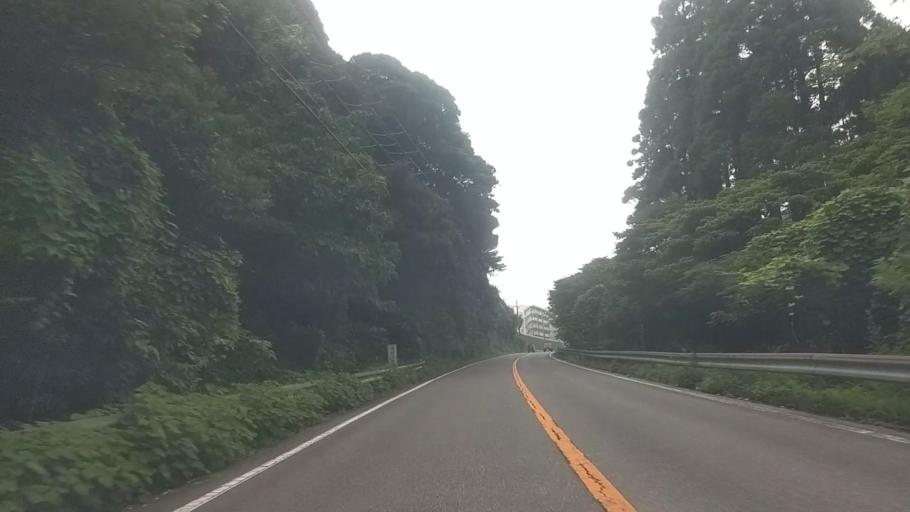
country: JP
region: Chiba
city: Katsuura
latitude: 35.1617
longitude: 140.3194
